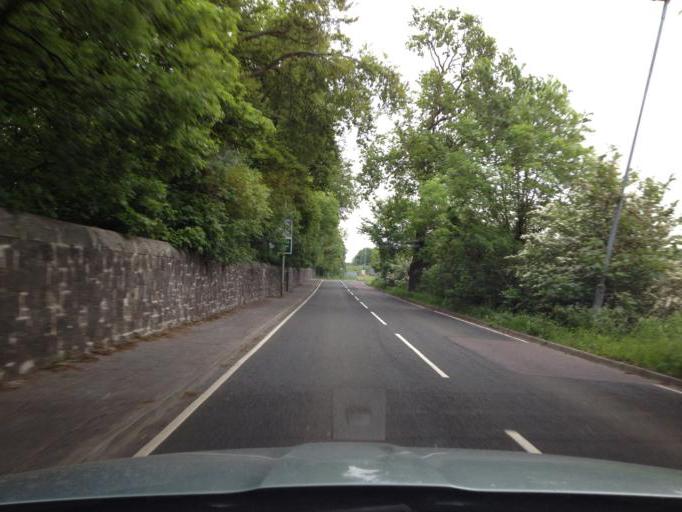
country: GB
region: Scotland
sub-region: West Dunbartonshire
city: Old Kilpatrick
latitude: 55.9141
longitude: -4.4780
